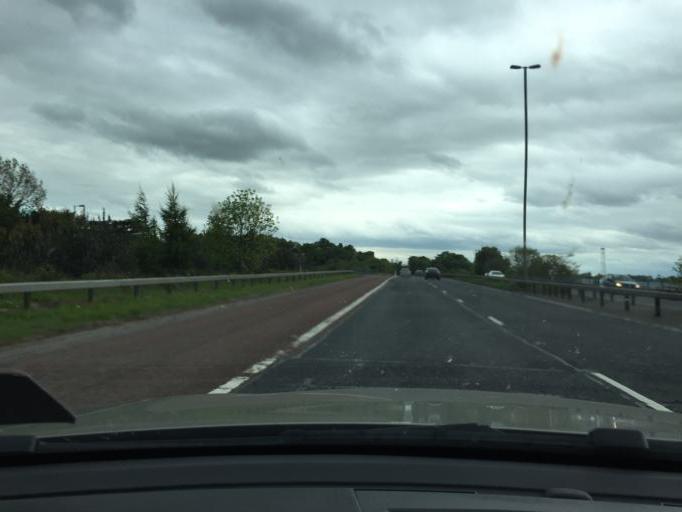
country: GB
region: Northern Ireland
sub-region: Lisburn District
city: Lisburn
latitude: 54.5589
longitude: -5.9948
